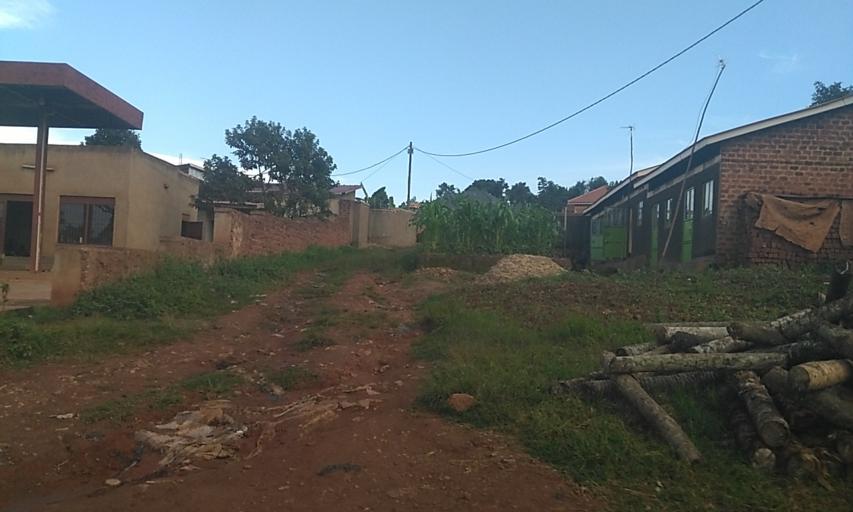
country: UG
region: Central Region
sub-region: Wakiso District
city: Kajansi
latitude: 0.2509
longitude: 32.5039
